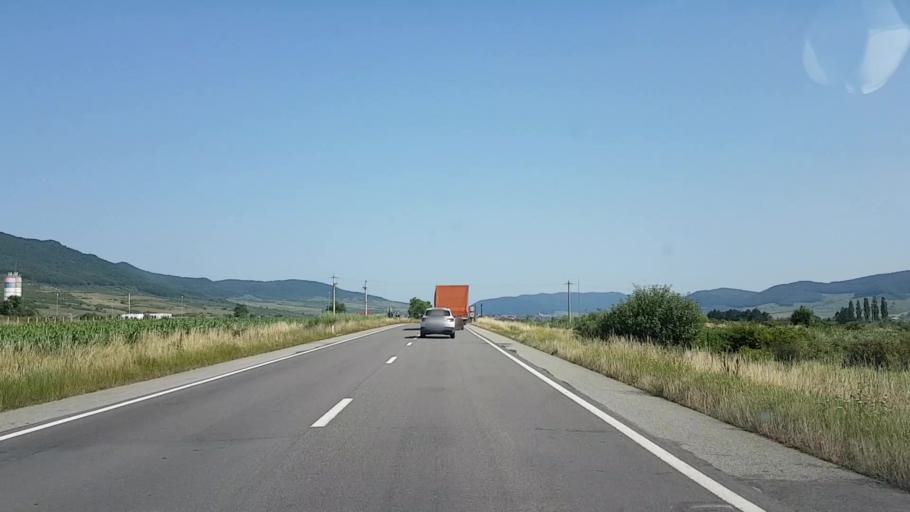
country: RO
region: Bistrita-Nasaud
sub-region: Comuna Sieu-Magherus
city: Sieu-Magherus
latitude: 47.1085
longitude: 24.3478
